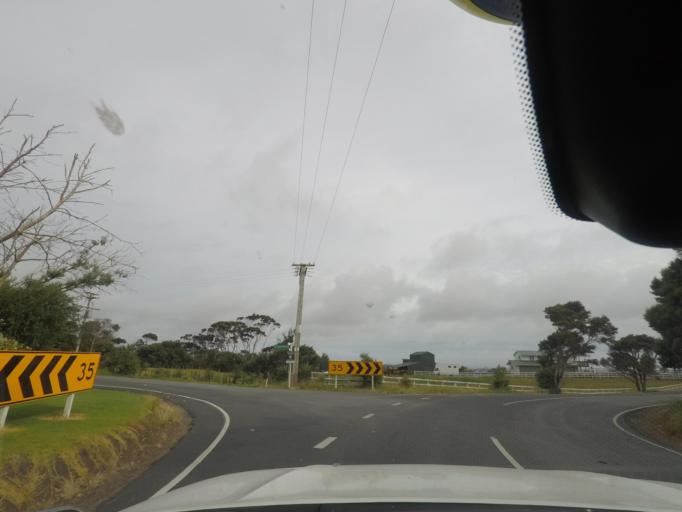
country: NZ
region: Auckland
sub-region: Auckland
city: Parakai
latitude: -36.4866
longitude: 174.2470
